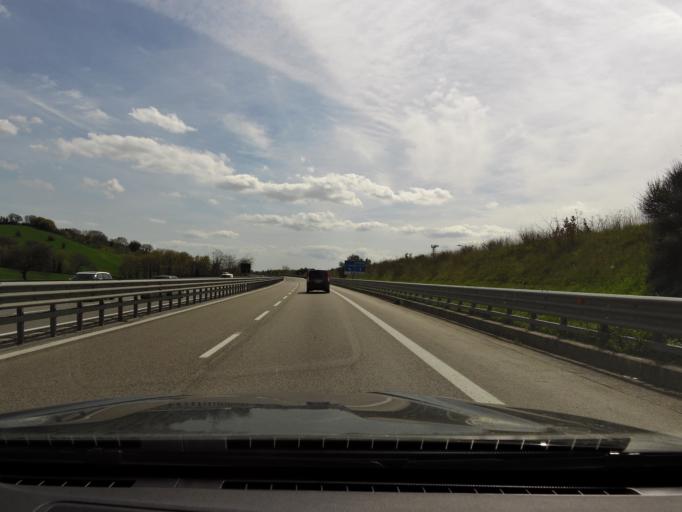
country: IT
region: The Marches
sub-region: Provincia di Ancona
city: San Biagio
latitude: 43.5400
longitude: 13.5149
